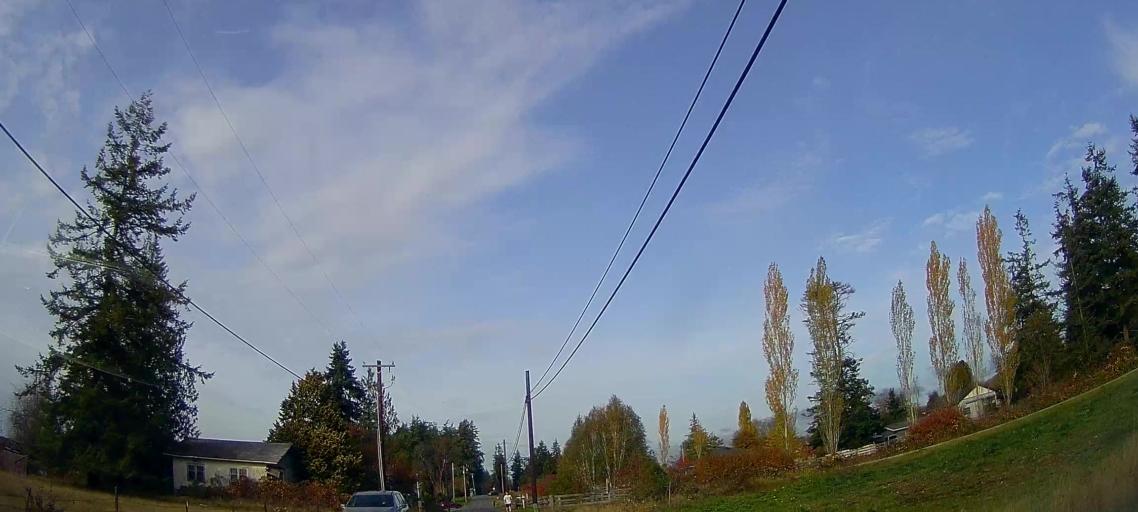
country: US
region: Washington
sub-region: Snohomish County
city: Stanwood
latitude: 48.2525
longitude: -122.3415
